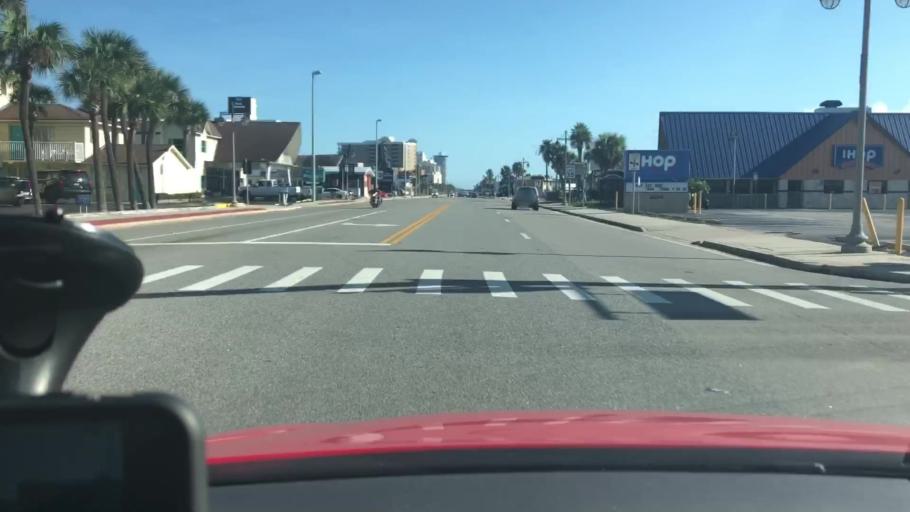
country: US
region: Florida
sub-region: Volusia County
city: Daytona Beach Shores
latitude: 29.1960
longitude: -80.9930
